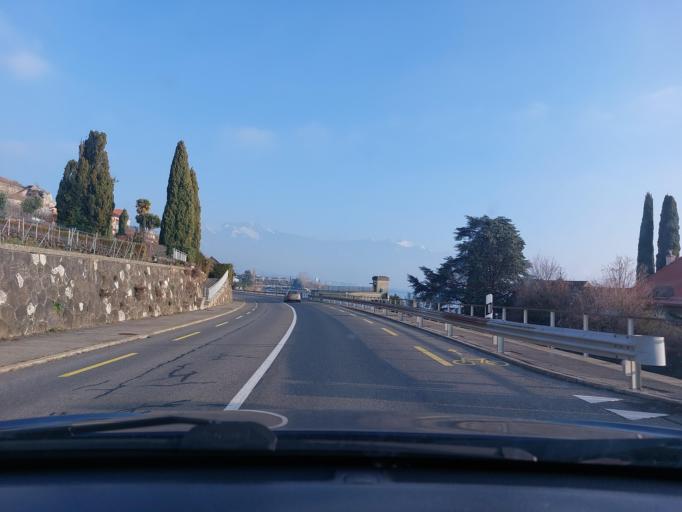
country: CH
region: Vaud
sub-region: Lavaux-Oron District
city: Chexbres
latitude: 46.4722
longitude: 6.8002
